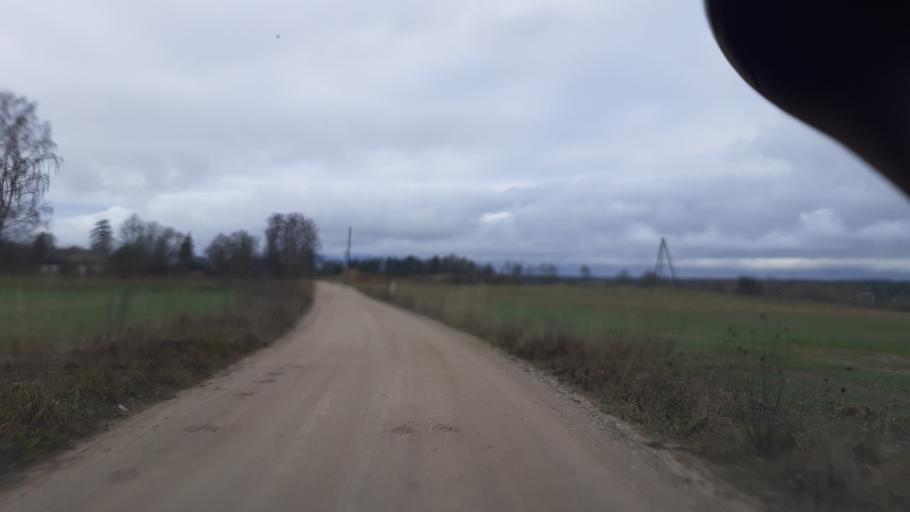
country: LV
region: Kuldigas Rajons
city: Kuldiga
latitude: 57.0438
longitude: 21.8716
